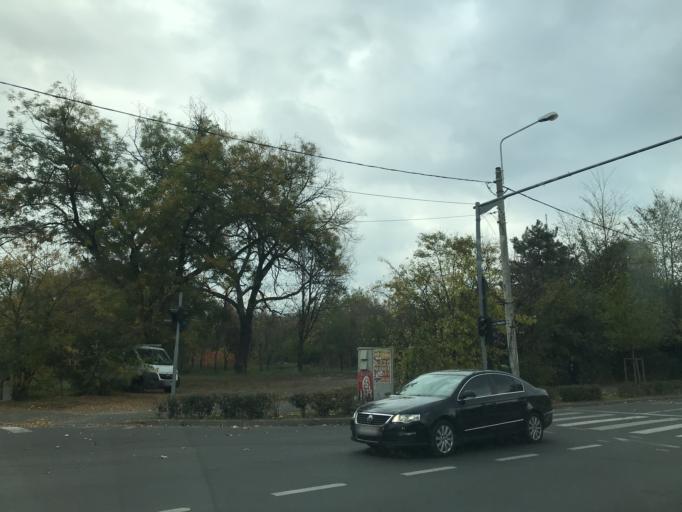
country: RO
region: Bucuresti
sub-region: Municipiul Bucuresti
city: Bucuresti
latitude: 44.4807
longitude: 26.0658
